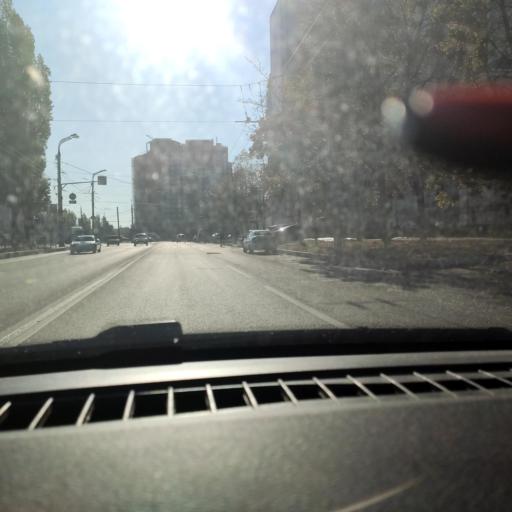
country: RU
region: Voronezj
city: Voronezh
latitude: 51.6519
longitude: 39.1624
